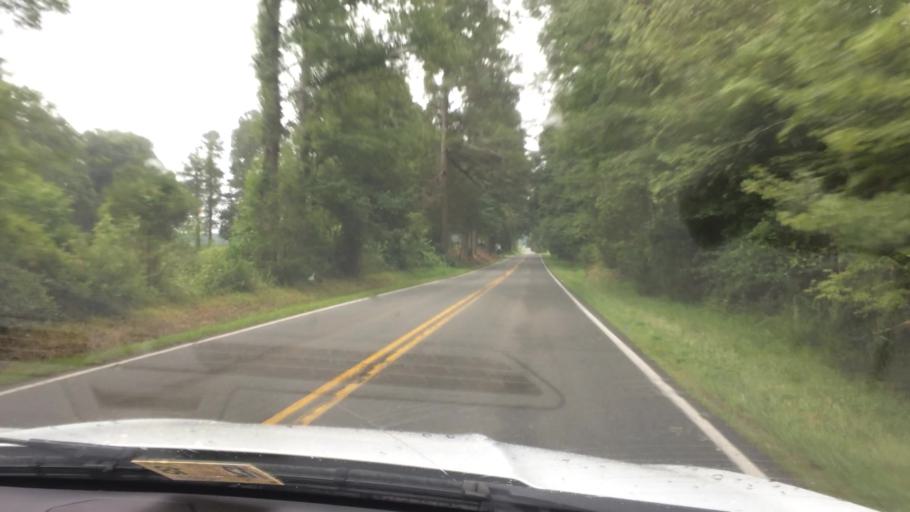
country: US
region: Virginia
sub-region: Charles City County
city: Charles City
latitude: 37.4232
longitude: -77.0402
